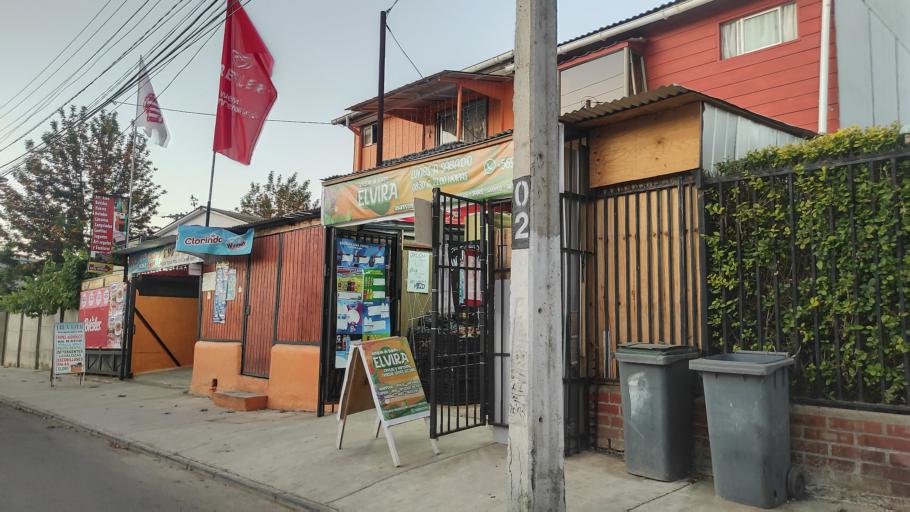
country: CL
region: Valparaiso
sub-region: Provincia de Marga Marga
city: Limache
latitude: -33.0203
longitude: -71.2640
